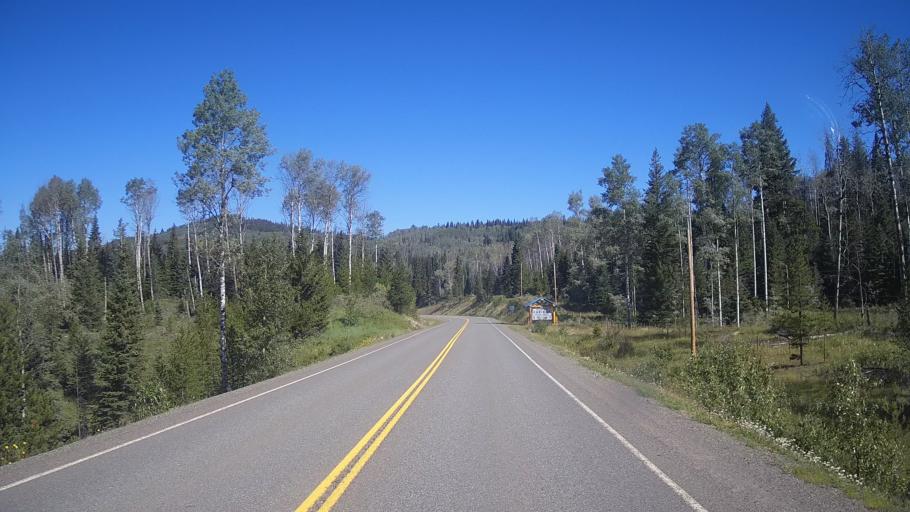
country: CA
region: British Columbia
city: Kamloops
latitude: 51.4872
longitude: -120.5642
